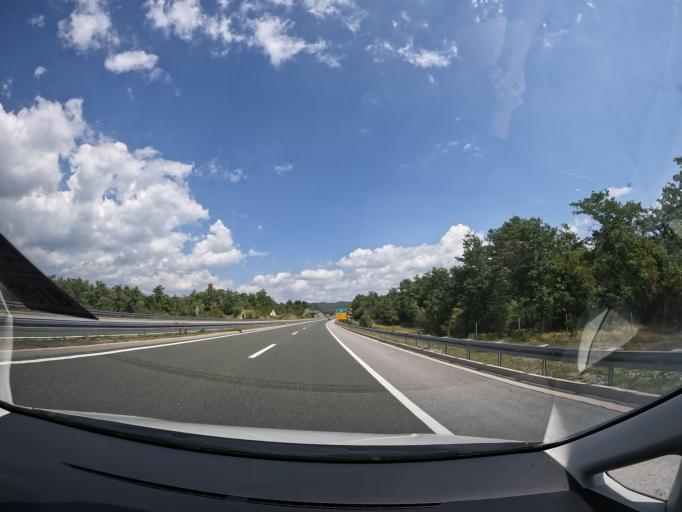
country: HR
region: Primorsko-Goranska
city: Klana
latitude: 45.4626
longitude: 14.2693
